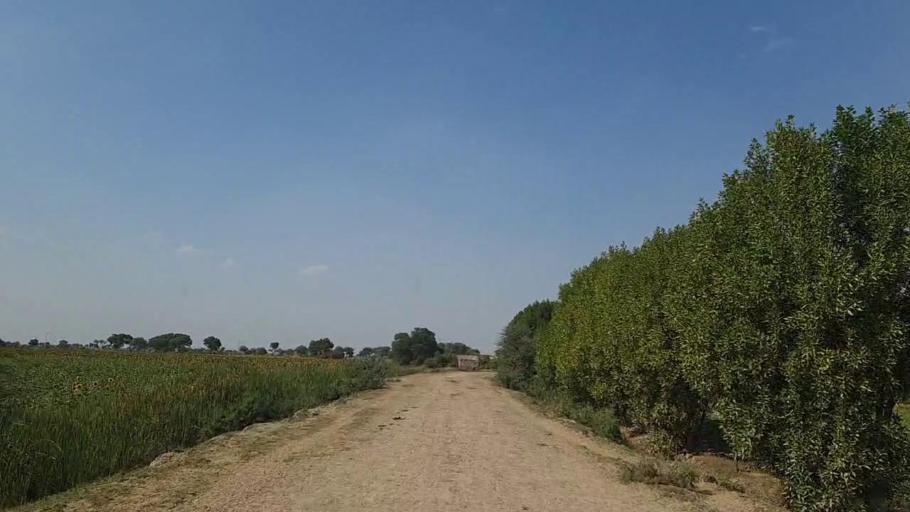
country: PK
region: Sindh
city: Jati
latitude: 24.5191
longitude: 68.2937
